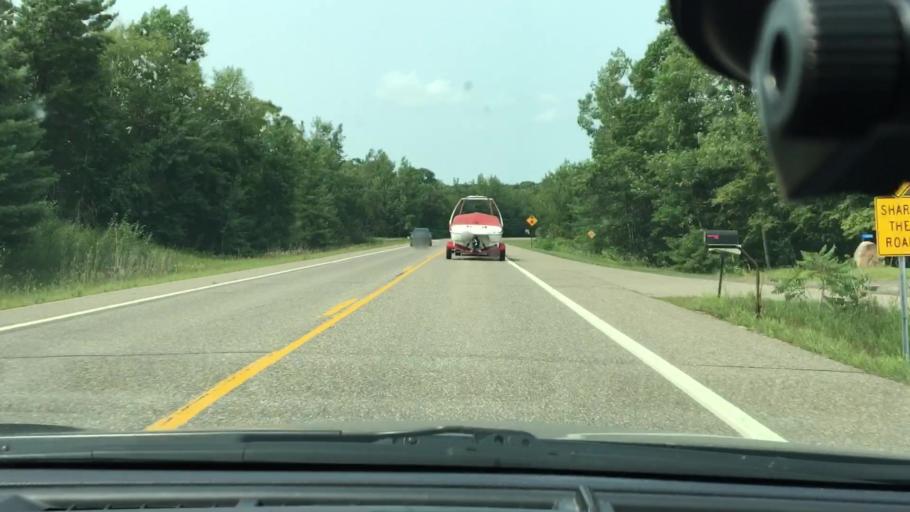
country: US
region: Minnesota
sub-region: Cass County
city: East Gull Lake
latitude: 46.4057
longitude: -94.3540
